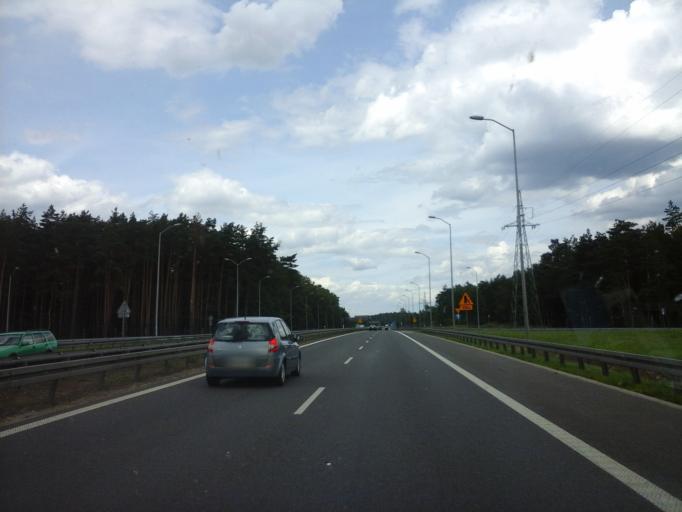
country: PL
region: West Pomeranian Voivodeship
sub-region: Powiat gryfinski
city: Stare Czarnowo
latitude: 53.3957
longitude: 14.7188
